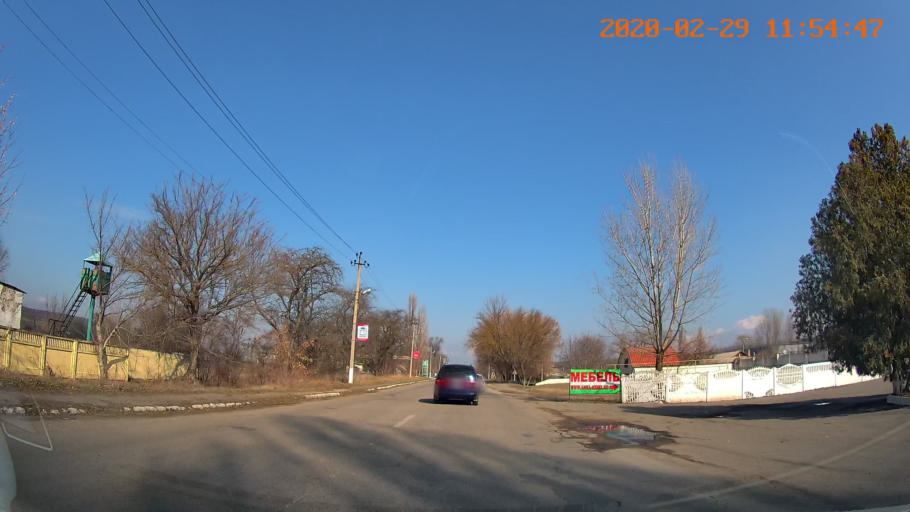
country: MD
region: Telenesti
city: Ribnita
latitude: 47.7863
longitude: 28.9961
